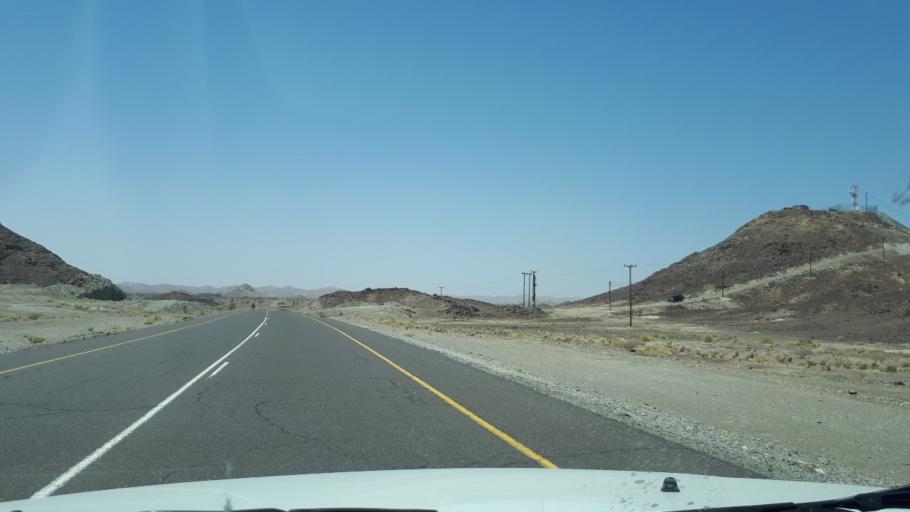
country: OM
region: Ash Sharqiyah
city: Ibra'
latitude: 22.6291
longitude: 58.4576
